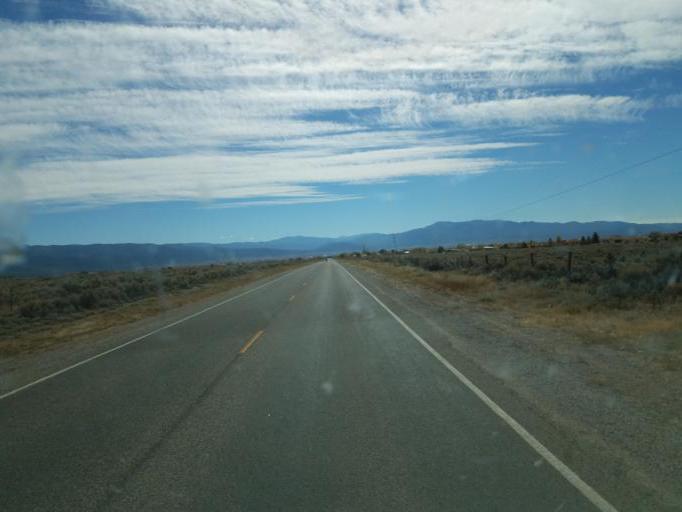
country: US
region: New Mexico
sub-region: Taos County
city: Arroyo Seco
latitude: 36.4805
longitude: -105.5937
